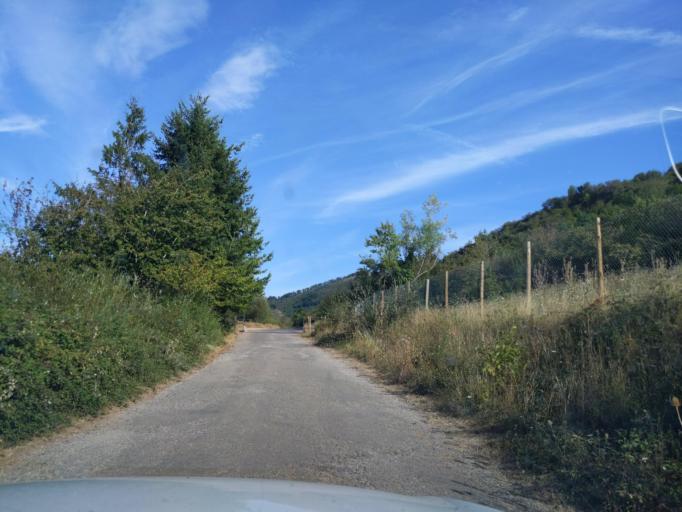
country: ES
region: La Rioja
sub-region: Provincia de La Rioja
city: Ezcaray
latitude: 42.3227
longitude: -3.0214
